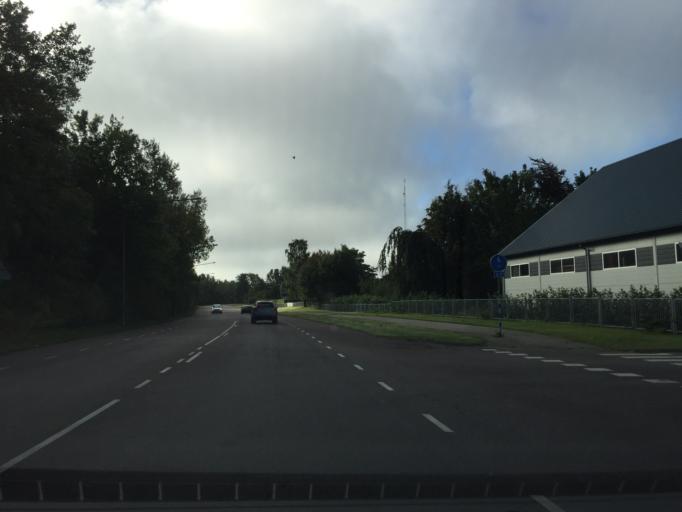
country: SE
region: Skane
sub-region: Staffanstorps Kommun
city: Staffanstorp
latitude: 55.6450
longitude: 13.1859
